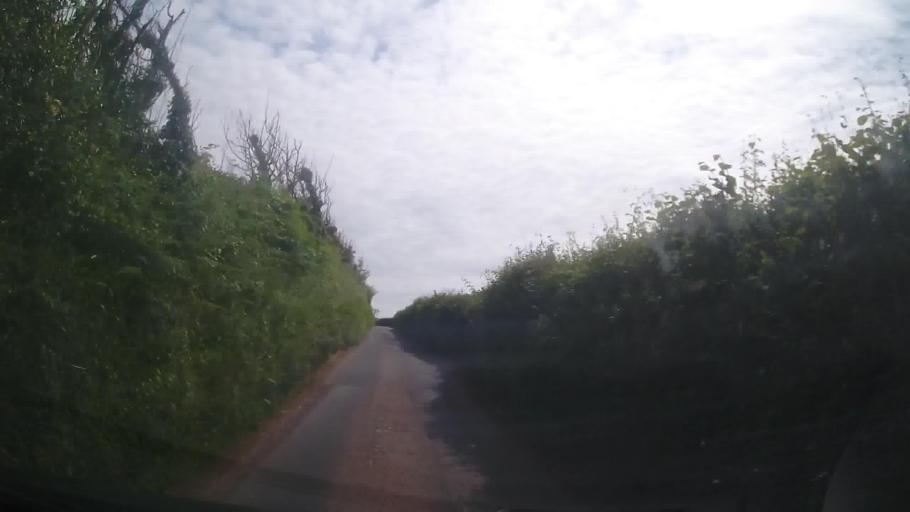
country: GB
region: England
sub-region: Devon
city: Salcombe
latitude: 50.2660
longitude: -3.6769
